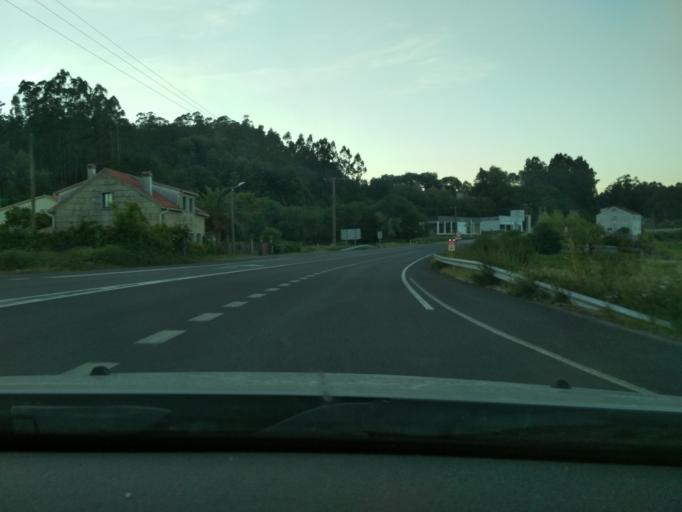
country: ES
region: Galicia
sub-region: Provincia de Pontevedra
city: Caldas de Reis
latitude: 42.6149
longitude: -8.6482
